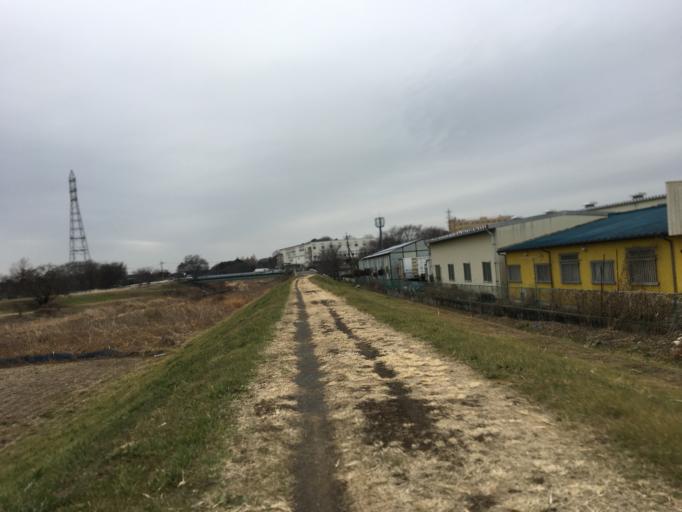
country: JP
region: Saitama
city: Oi
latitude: 35.8060
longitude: 139.5394
